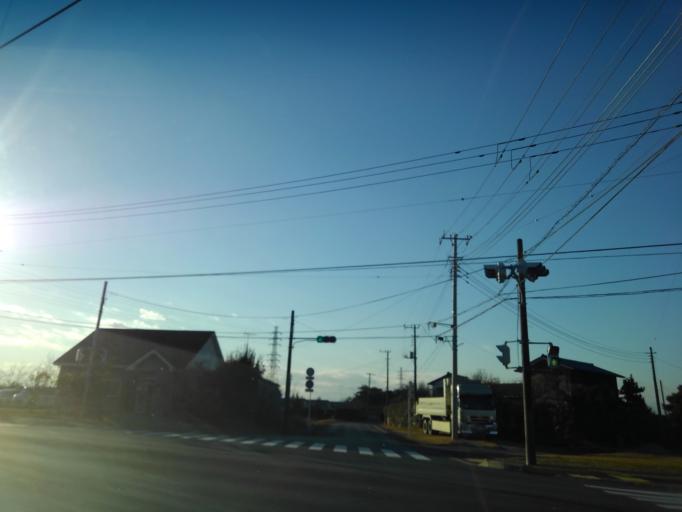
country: JP
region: Chiba
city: Kimitsu
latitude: 35.3217
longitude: 139.9069
